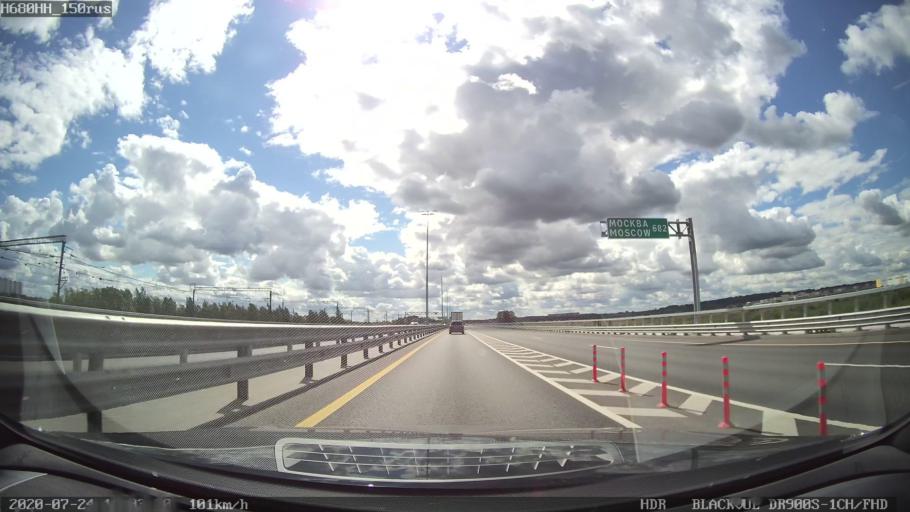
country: RU
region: St.-Petersburg
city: Shushary
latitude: 59.8018
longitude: 30.3380
